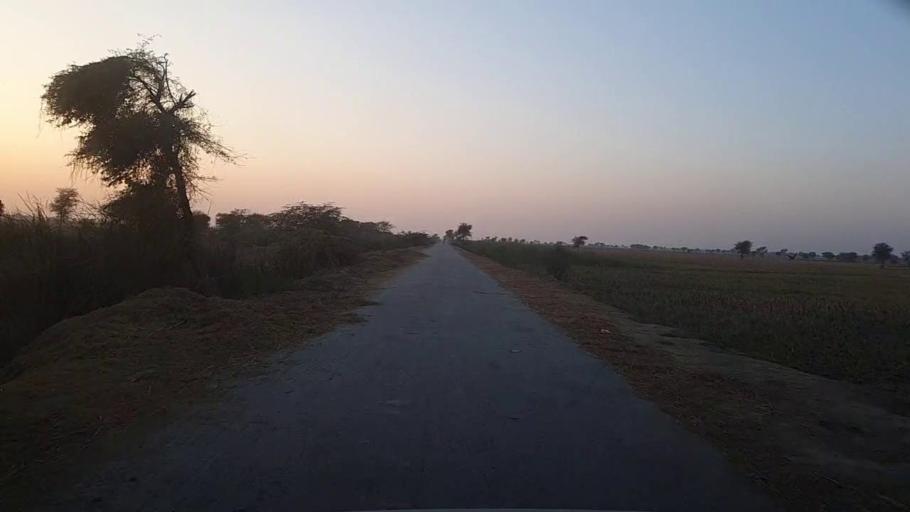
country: PK
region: Sindh
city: Khairpur Nathan Shah
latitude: 27.1586
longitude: 67.7124
